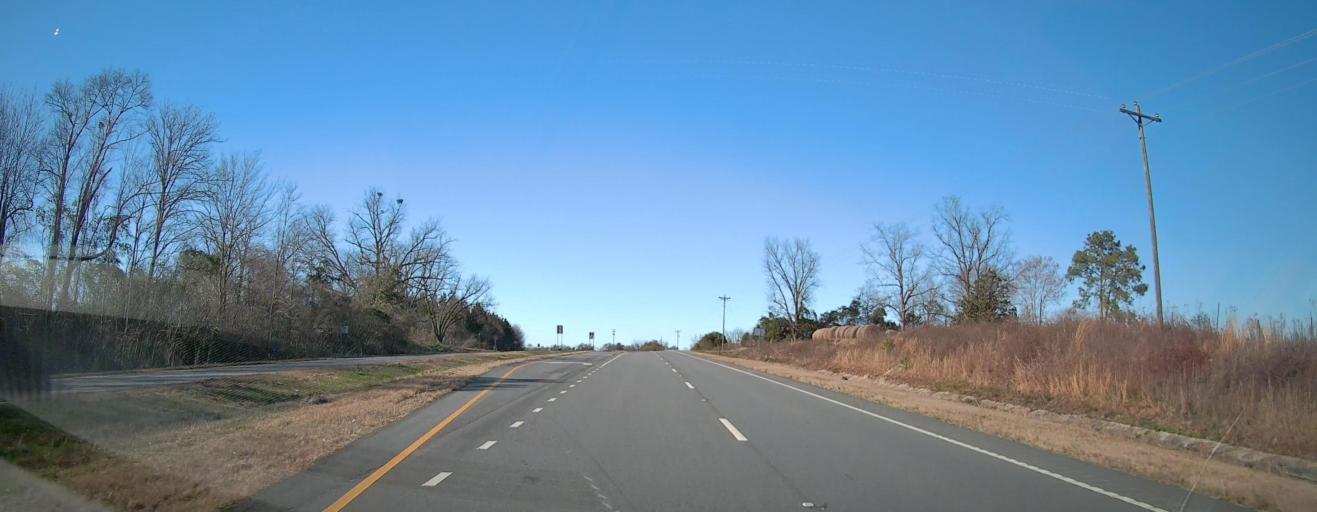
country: US
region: Georgia
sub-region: Taylor County
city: Butler
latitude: 32.6215
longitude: -84.2477
